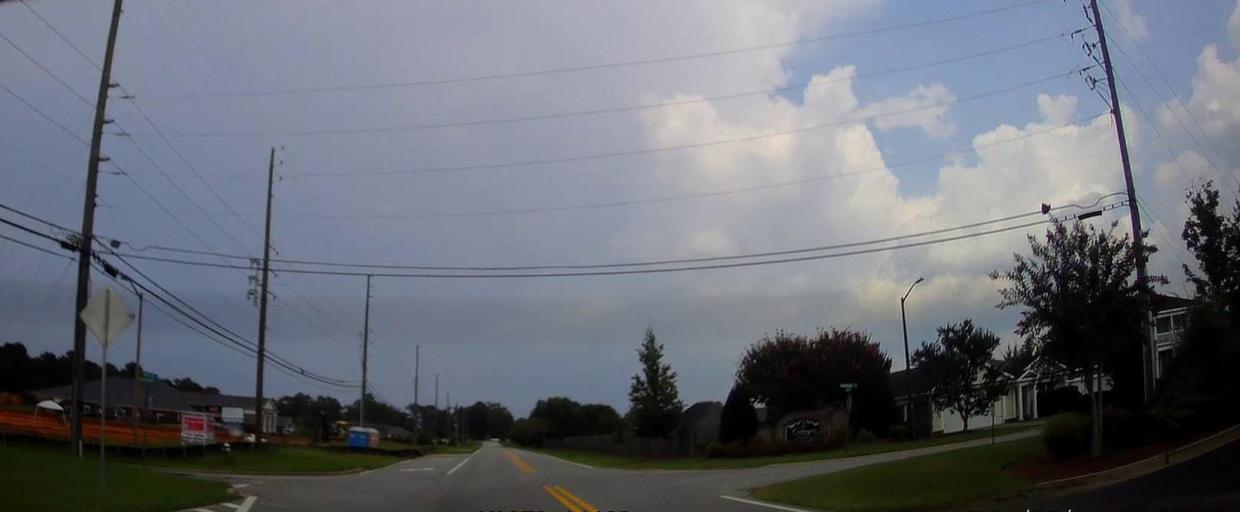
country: US
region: Georgia
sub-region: Houston County
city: Robins Air Force Base
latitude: 32.5683
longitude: -83.5931
